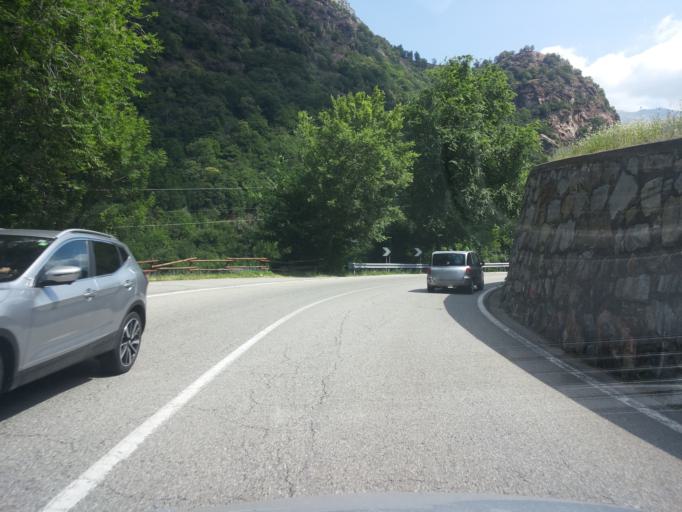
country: IT
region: Aosta Valley
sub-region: Valle d'Aosta
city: Perloz
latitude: 45.6223
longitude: 7.8229
